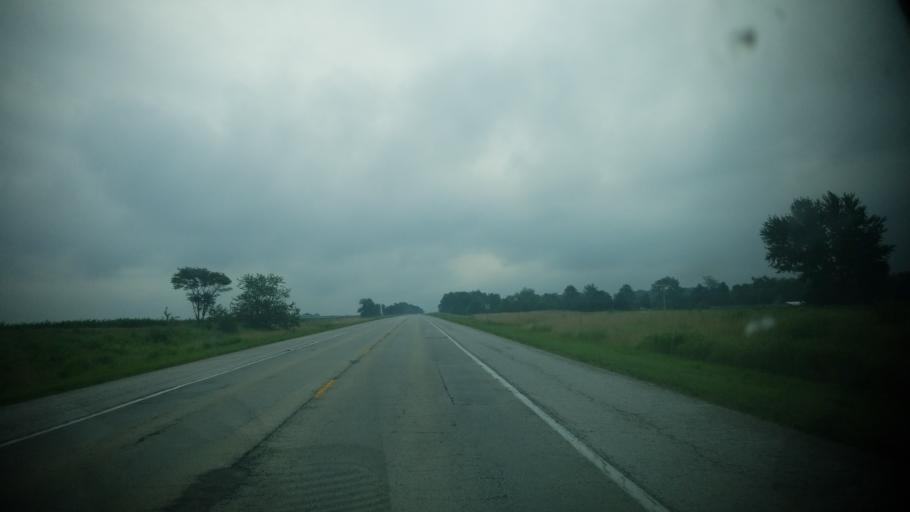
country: US
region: Illinois
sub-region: Clay County
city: Flora
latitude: 38.6773
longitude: -88.4068
